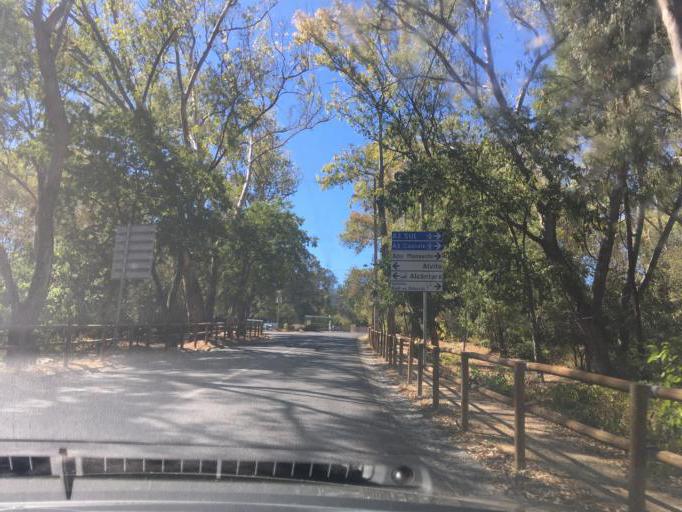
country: PT
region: Setubal
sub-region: Almada
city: Pragal
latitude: 38.7198
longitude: -9.1836
